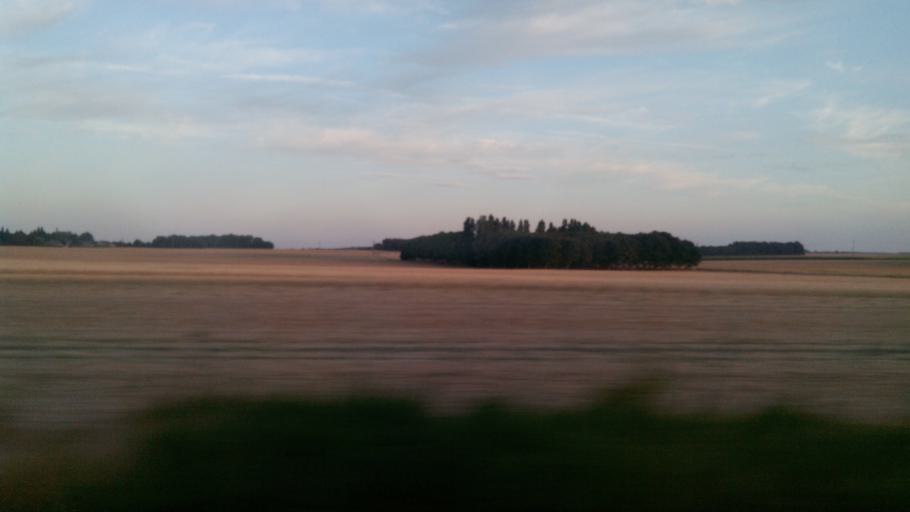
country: FR
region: Centre
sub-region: Departement d'Eure-et-Loir
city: Yevres
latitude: 48.1339
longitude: 1.1996
